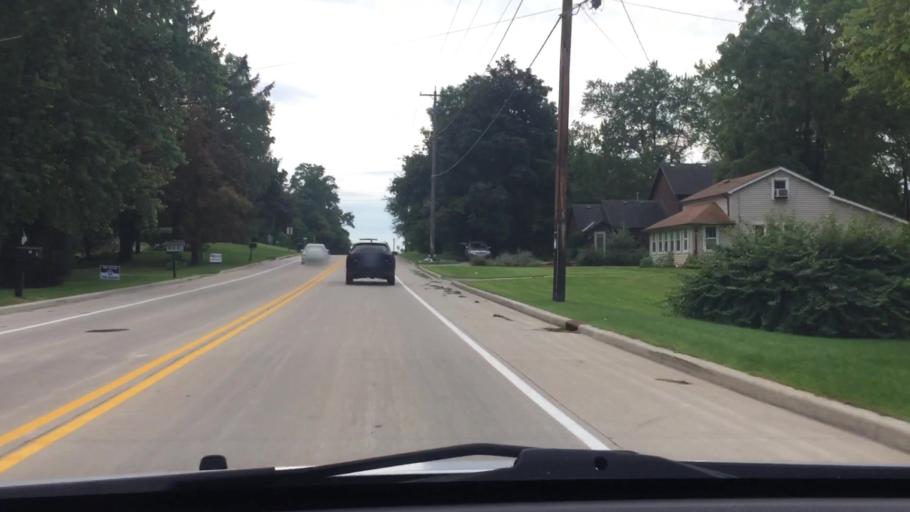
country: US
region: Wisconsin
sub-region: Waukesha County
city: North Prairie
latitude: 42.9533
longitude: -88.3572
